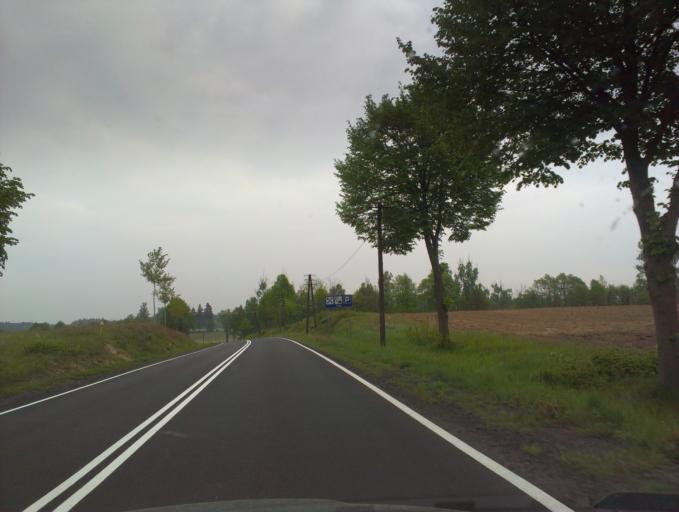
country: PL
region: West Pomeranian Voivodeship
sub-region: Powiat szczecinecki
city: Szczecinek
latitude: 53.8073
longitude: 16.6425
